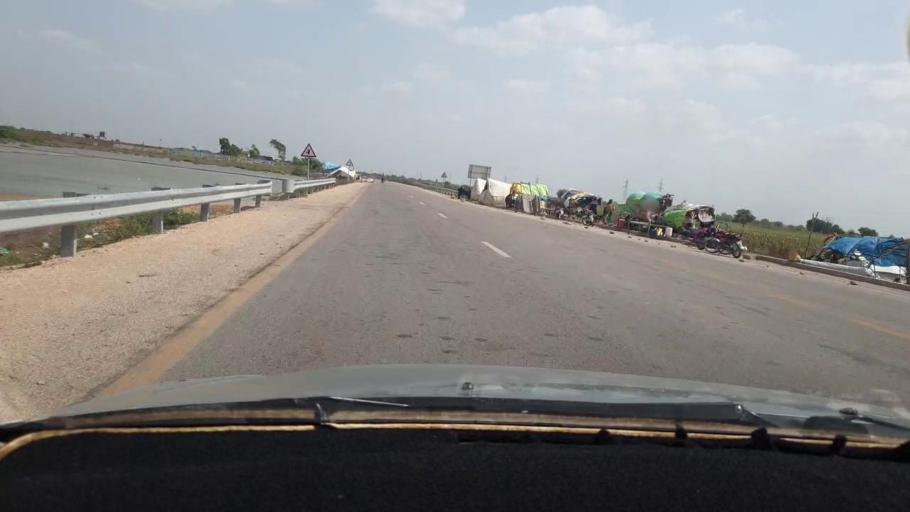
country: PK
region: Sindh
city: Digri
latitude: 25.0514
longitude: 69.2229
